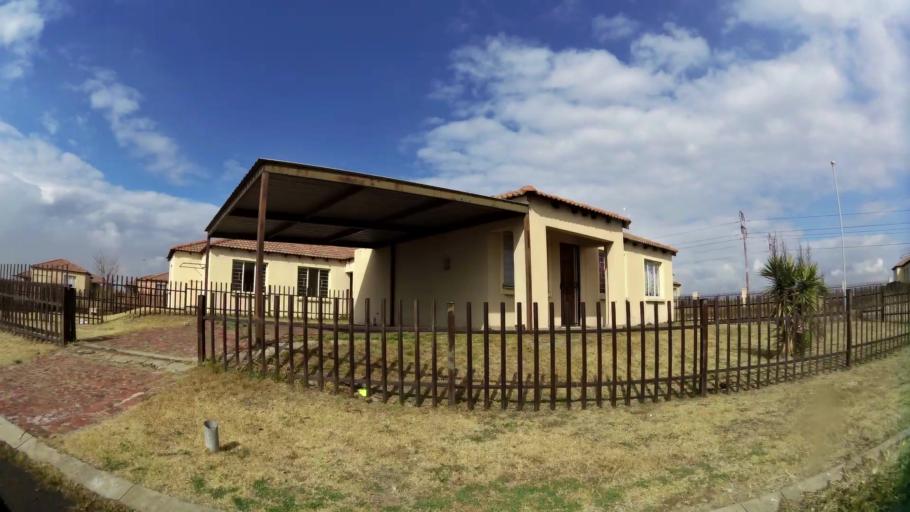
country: ZA
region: Gauteng
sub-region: Sedibeng District Municipality
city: Vanderbijlpark
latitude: -26.7153
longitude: 27.8807
